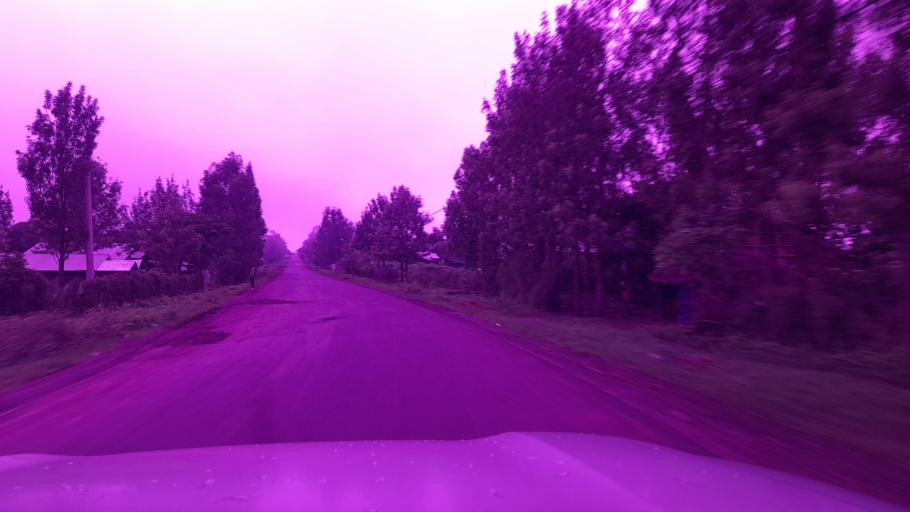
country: ET
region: Oromiya
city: Waliso
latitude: 8.1743
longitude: 37.5665
